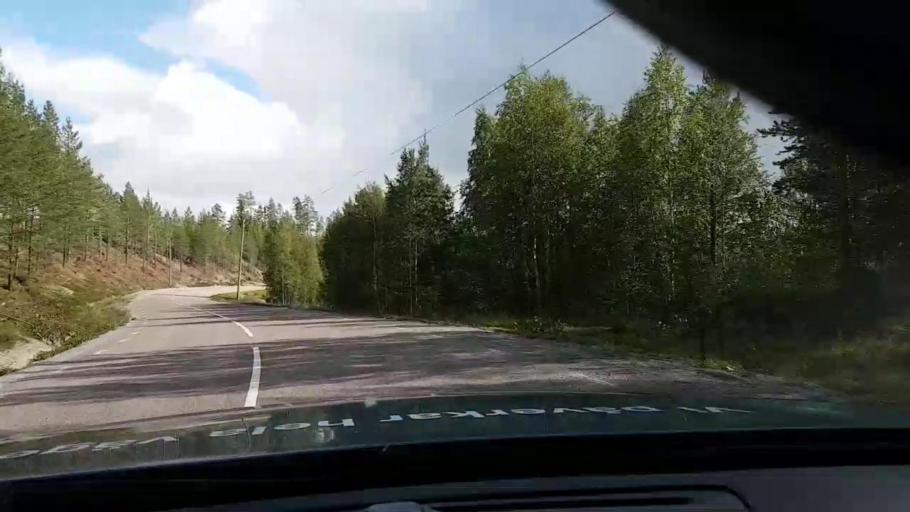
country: SE
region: Vaesterbotten
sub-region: Asele Kommun
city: Asele
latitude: 63.8664
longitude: 17.3622
